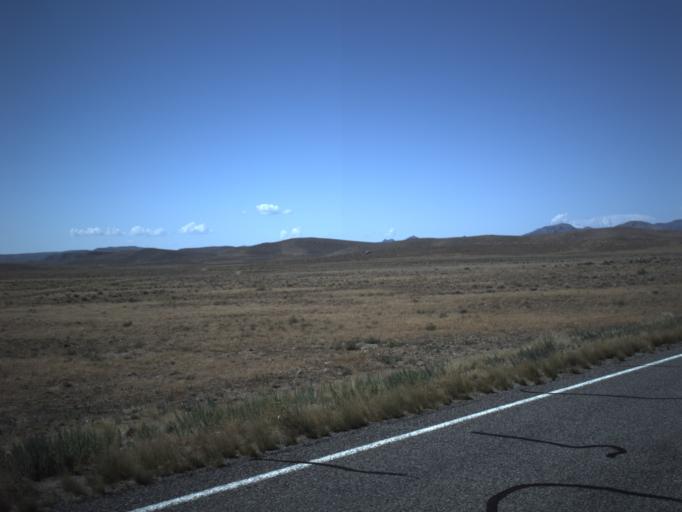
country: US
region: Utah
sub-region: Beaver County
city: Milford
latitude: 39.0418
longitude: -113.2968
